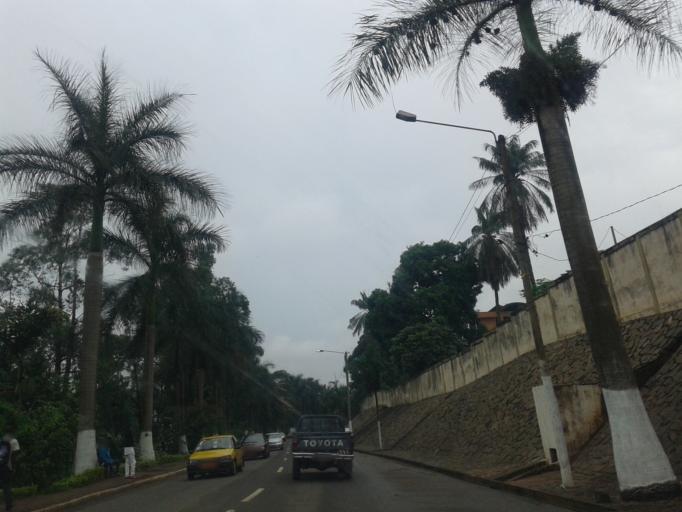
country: CM
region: Centre
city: Yaounde
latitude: 3.8739
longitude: 11.5140
